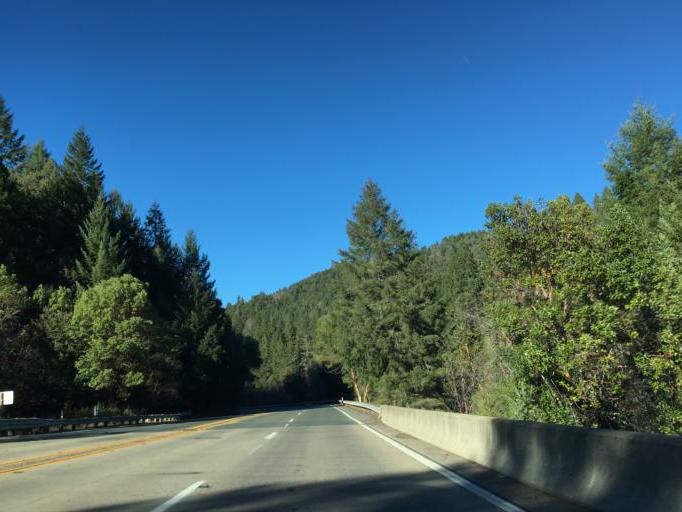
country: US
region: California
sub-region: Mendocino County
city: Laytonville
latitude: 39.5815
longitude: -123.4443
